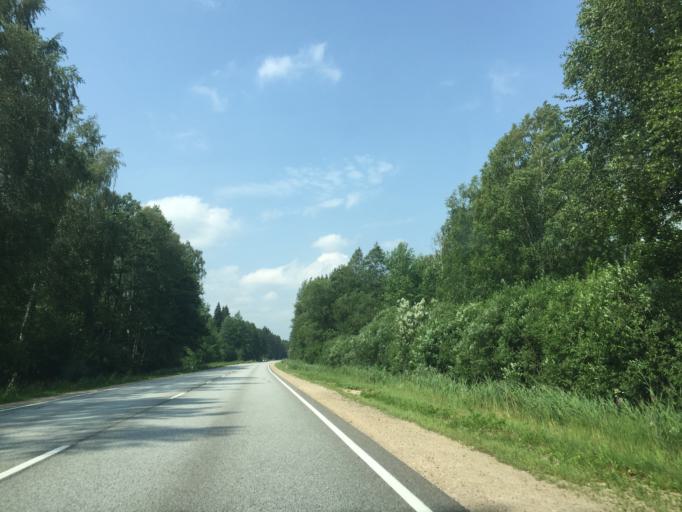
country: LV
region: Kekava
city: Balozi
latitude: 56.8246
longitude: 24.0691
